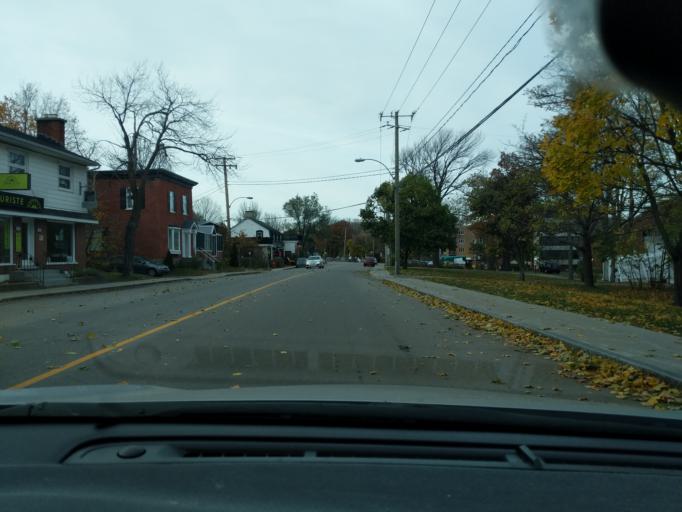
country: CA
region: Quebec
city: Quebec
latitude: 46.7830
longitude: -71.2460
